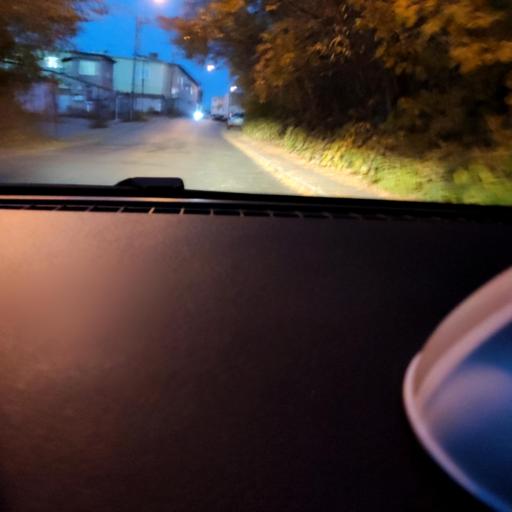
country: RU
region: Samara
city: Samara
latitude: 53.1865
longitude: 50.1472
